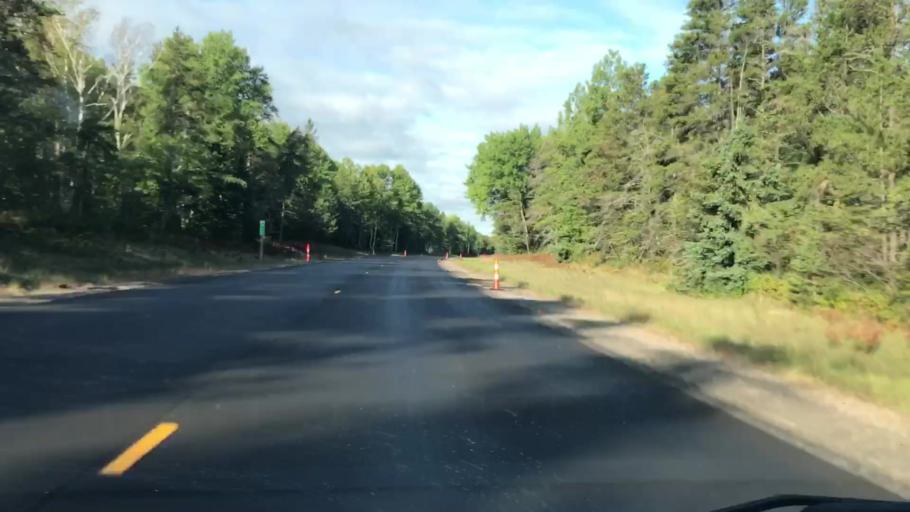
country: US
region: Michigan
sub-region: Mackinac County
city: Saint Ignace
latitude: 46.3461
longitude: -84.9224
